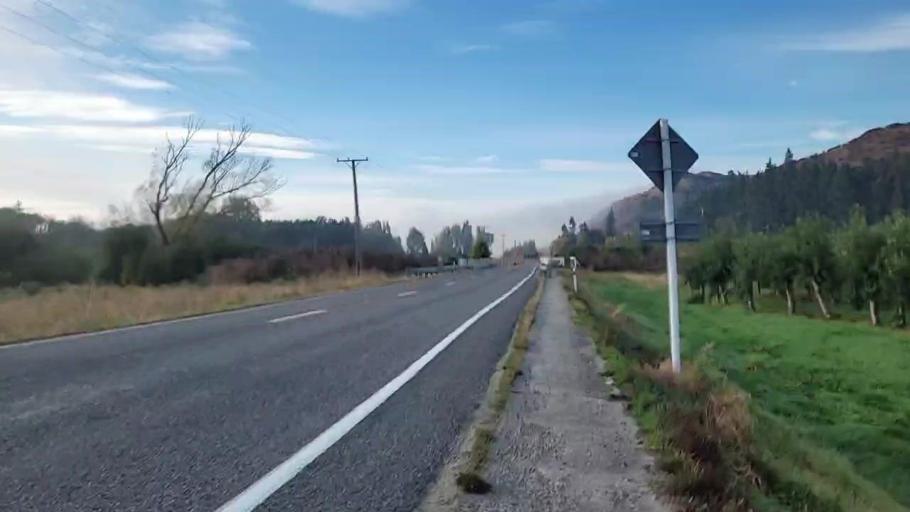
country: NZ
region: Southland
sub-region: Gore District
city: Gore
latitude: -45.6422
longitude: 169.3743
